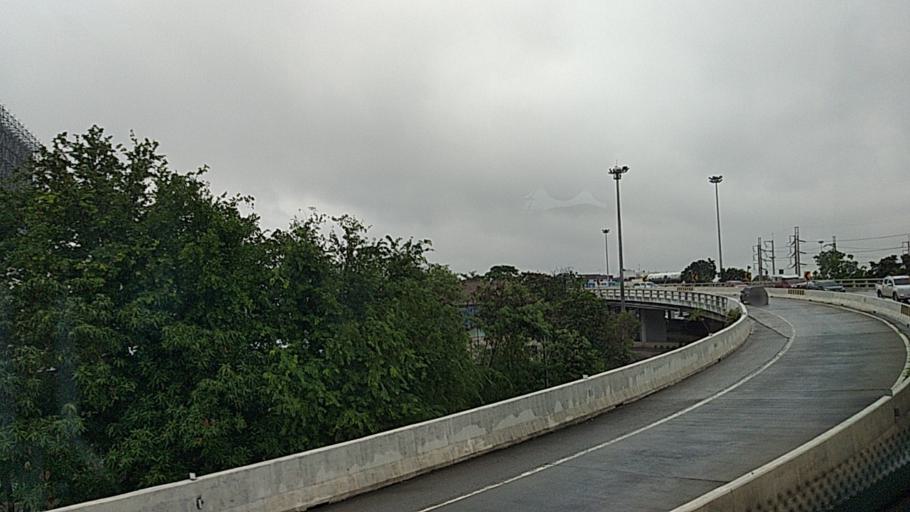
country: TH
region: Nakhon Ratchasima
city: Nakhon Ratchasima
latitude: 14.9578
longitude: 102.0524
